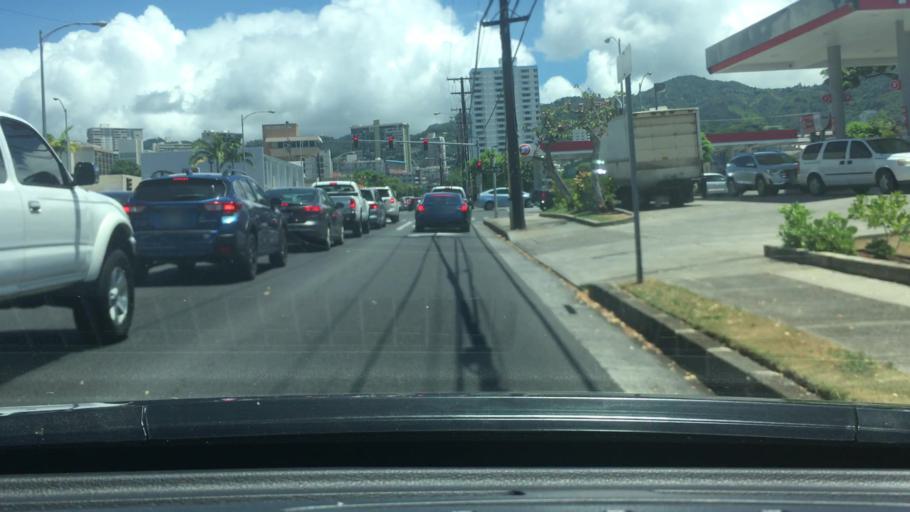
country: US
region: Hawaii
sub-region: Honolulu County
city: Honolulu
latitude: 21.2993
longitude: -157.8443
